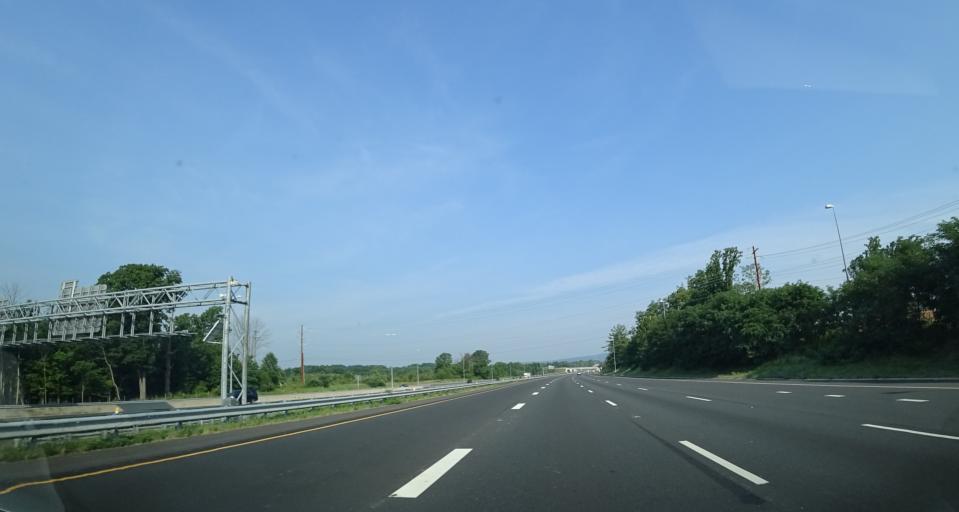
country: US
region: Virginia
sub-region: Prince William County
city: Gainesville
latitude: 38.8018
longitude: -77.6056
